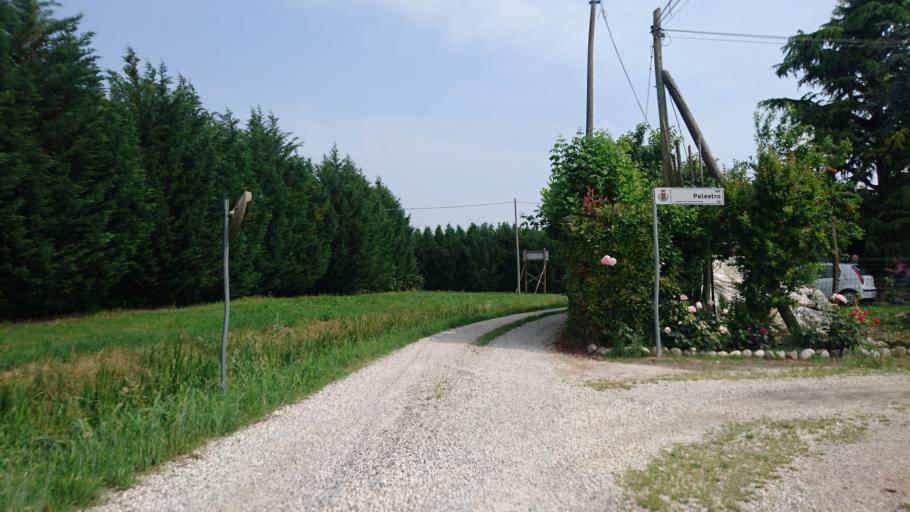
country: IT
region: Veneto
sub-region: Provincia di Padova
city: Ponte San Nicolo
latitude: 45.3537
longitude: 11.9397
